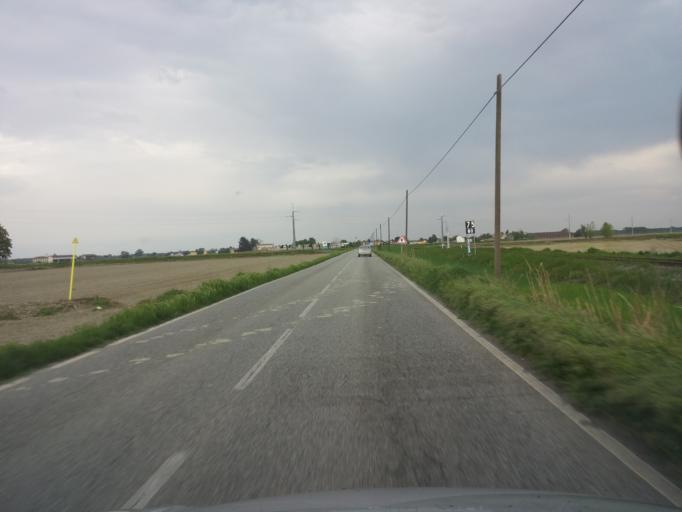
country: IT
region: Piedmont
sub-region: Provincia di Alessandria
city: Villanova Monferrato
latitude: 45.1629
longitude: 8.5044
